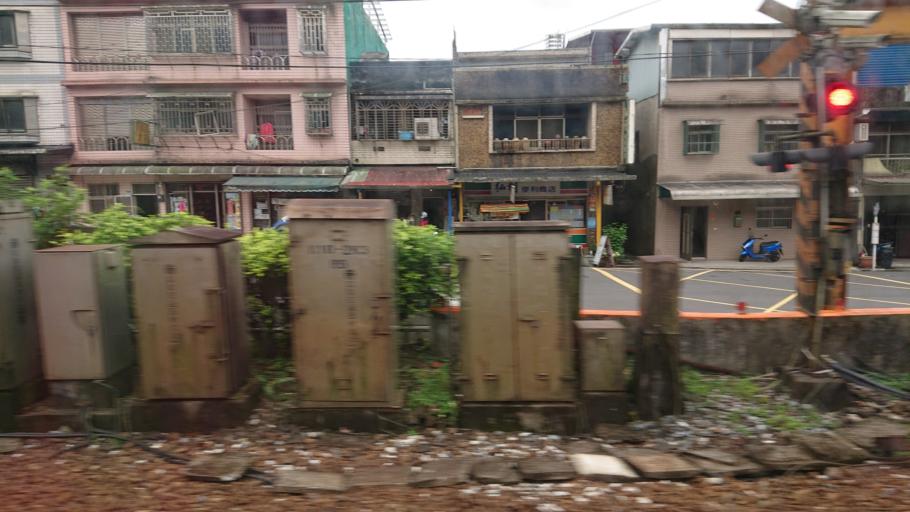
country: TW
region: Taiwan
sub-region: Keelung
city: Keelung
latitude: 25.1077
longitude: 121.8194
